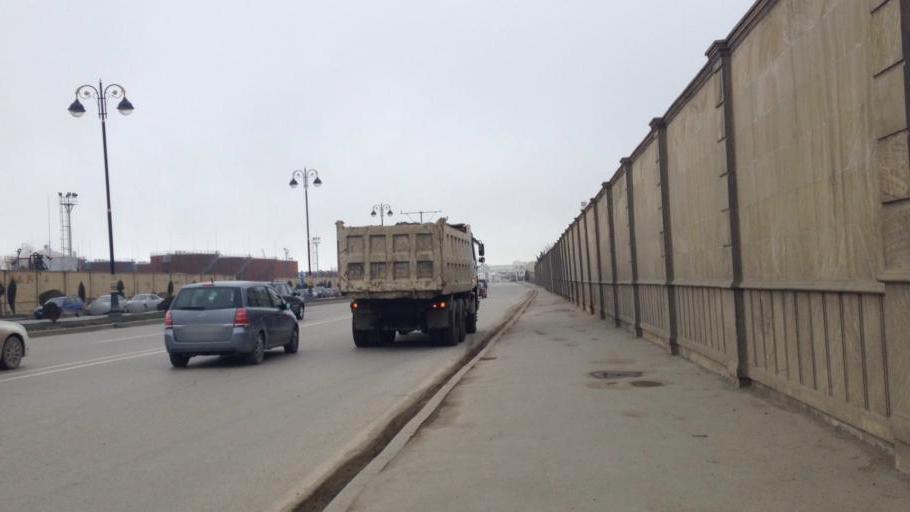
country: AZ
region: Baki
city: Baku
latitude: 40.3767
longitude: 49.9123
